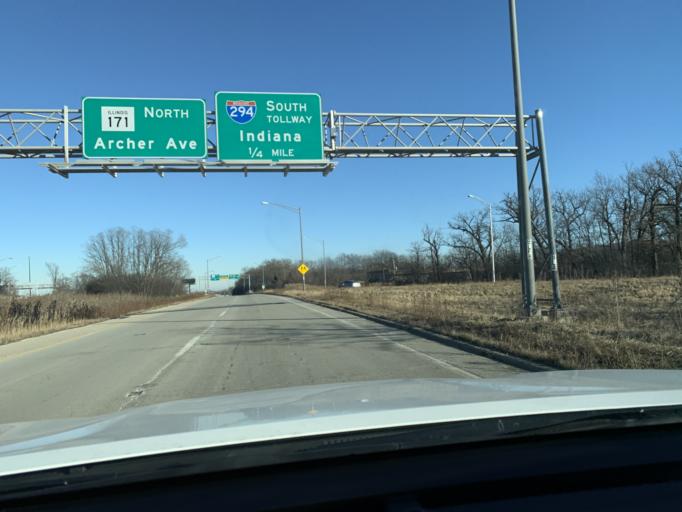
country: US
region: Illinois
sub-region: Cook County
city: Willow Springs
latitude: 41.7441
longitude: -87.8499
